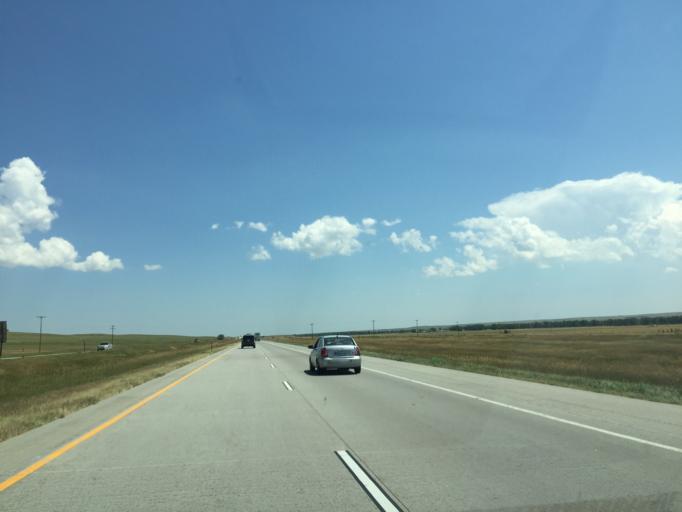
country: US
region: Colorado
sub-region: Lincoln County
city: Limon
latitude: 39.3002
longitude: -103.8112
